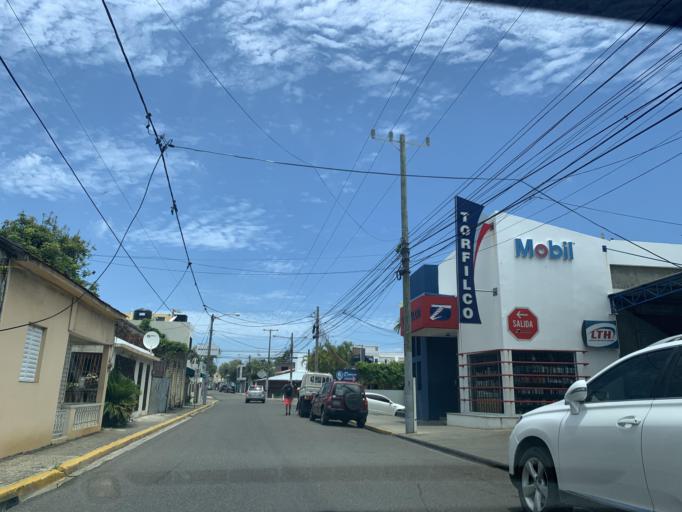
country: DO
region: Puerto Plata
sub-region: Puerto Plata
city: Puerto Plata
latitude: 19.7953
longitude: -70.6858
